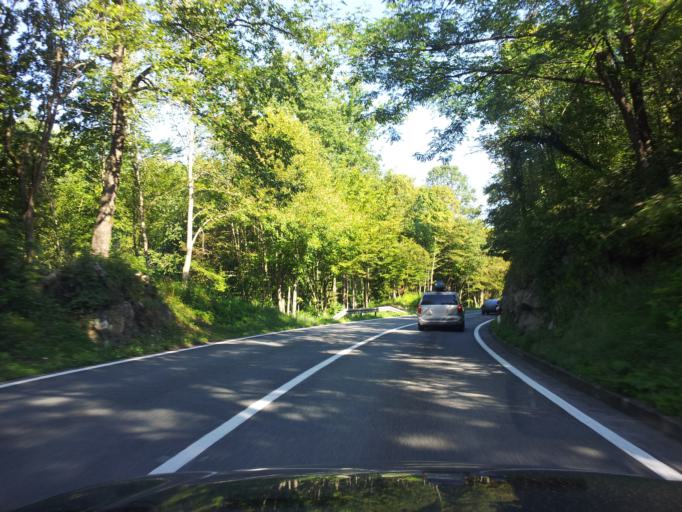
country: HR
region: Karlovacka
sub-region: Grad Karlovac
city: Slunj
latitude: 45.1944
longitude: 15.5556
